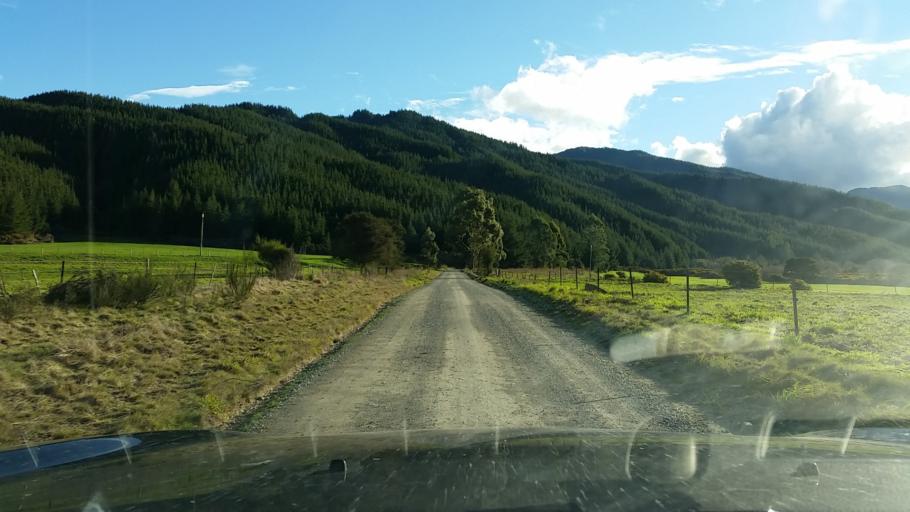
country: NZ
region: Nelson
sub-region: Nelson City
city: Nelson
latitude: -41.5649
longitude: 173.4464
